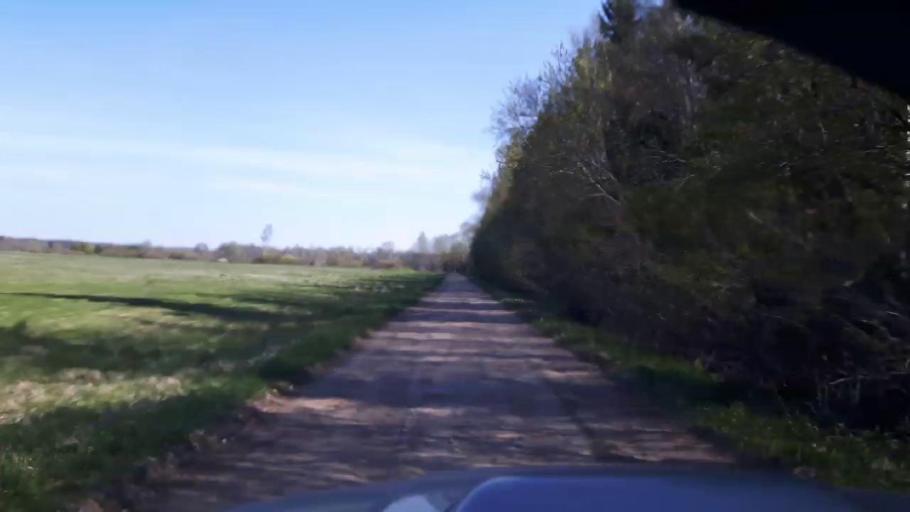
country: EE
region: Paernumaa
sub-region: Tootsi vald
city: Tootsi
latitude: 58.4842
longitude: 24.9292
